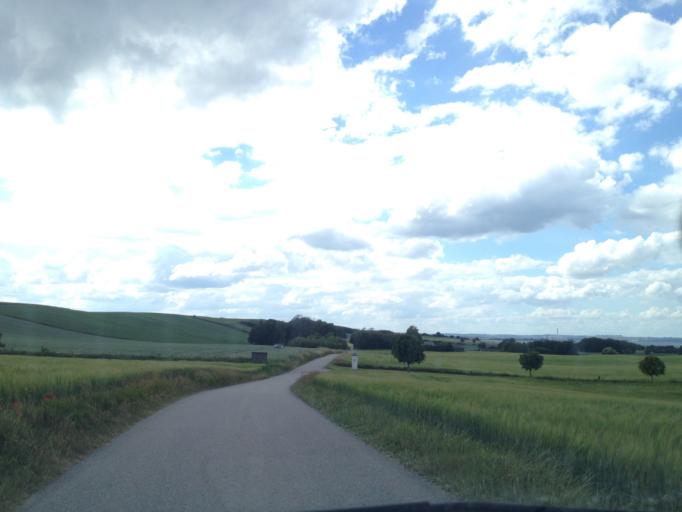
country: DK
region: Central Jutland
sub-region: Syddjurs Kommune
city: Ronde
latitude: 56.1963
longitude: 10.5037
